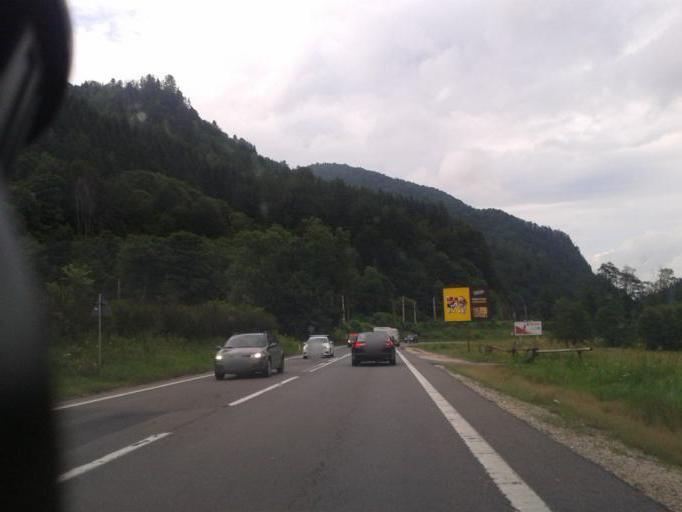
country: RO
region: Brasov
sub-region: Oras Predeal
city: Predeal
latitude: 45.5536
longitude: 25.5911
